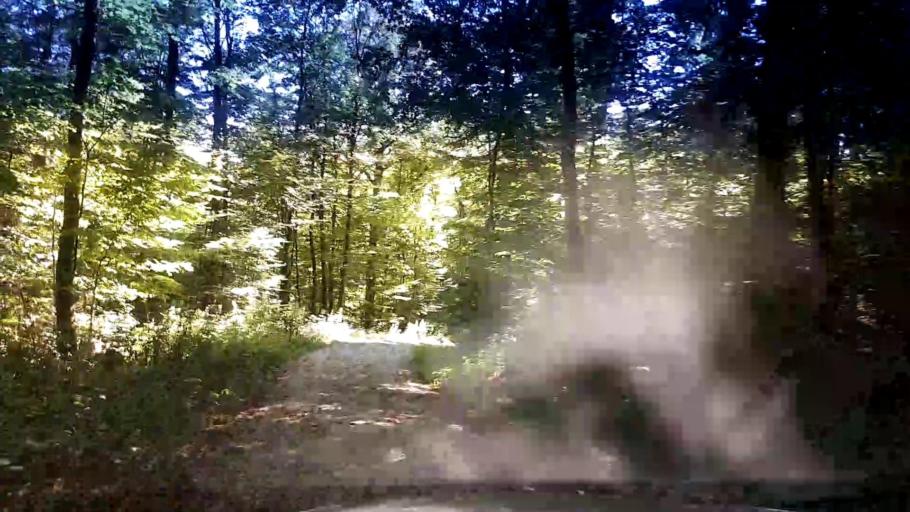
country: DE
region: Bavaria
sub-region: Upper Franconia
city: Litzendorf
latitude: 49.8837
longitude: 11.0295
